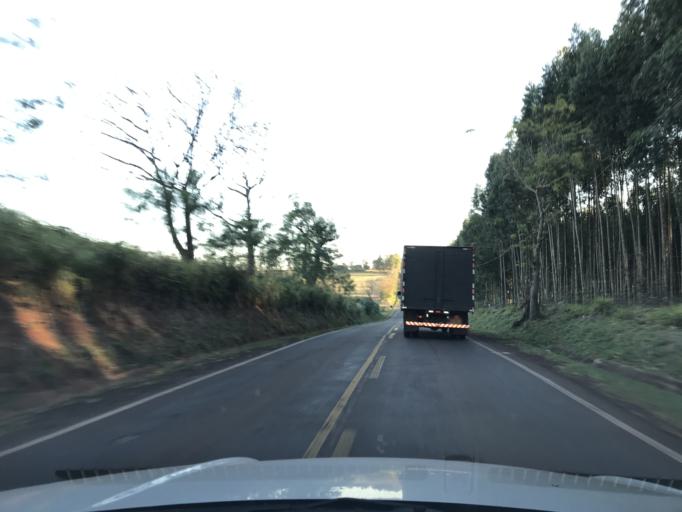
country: PY
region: Canindeyu
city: Salto del Guaira
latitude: -24.0969
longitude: -54.0993
